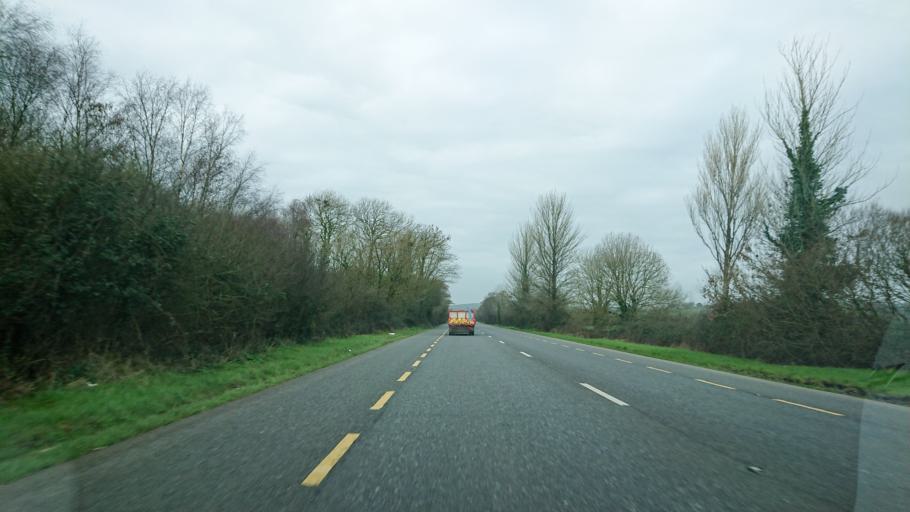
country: IE
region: Munster
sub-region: County Cork
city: Castlemartyr
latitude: 51.9392
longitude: -7.9742
